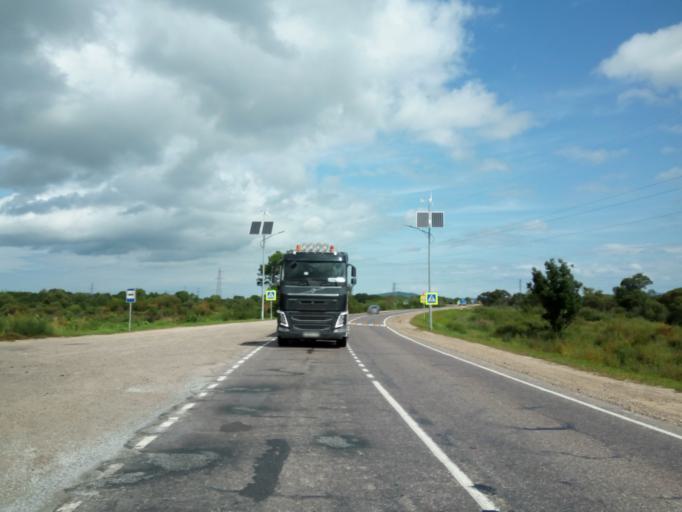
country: RU
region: Primorskiy
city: Dal'nerechensk
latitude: 45.9664
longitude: 133.7830
